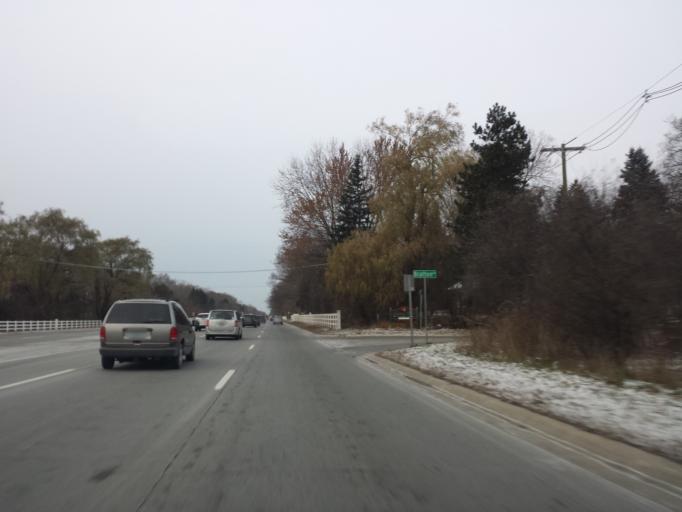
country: US
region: Michigan
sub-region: Oakland County
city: Bloomfield Hills
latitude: 42.6035
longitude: -83.2694
